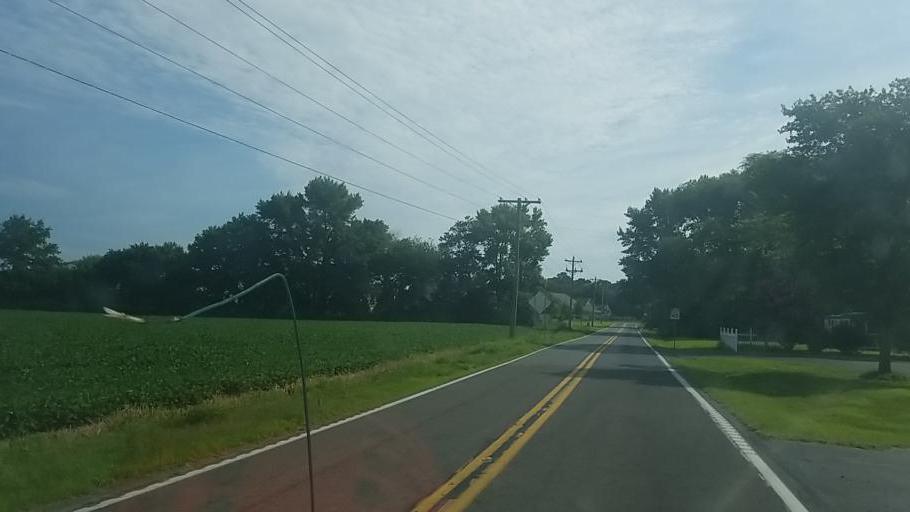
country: US
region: Delaware
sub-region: Sussex County
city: Ocean View
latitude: 38.5051
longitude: -75.1229
